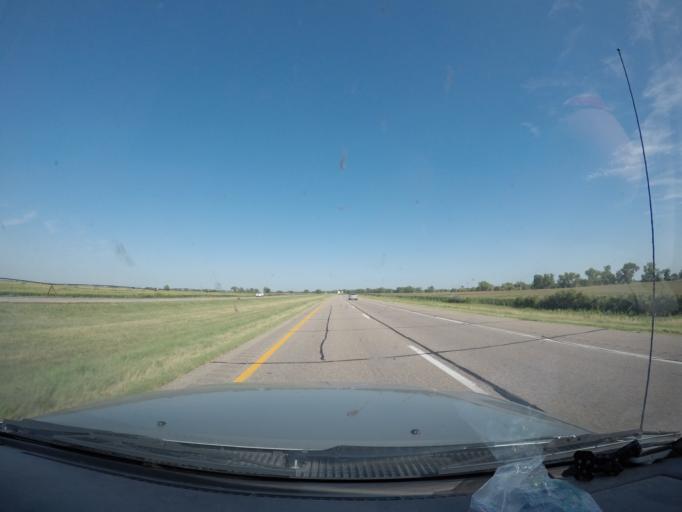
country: US
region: Nebraska
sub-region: Buffalo County
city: Kearney
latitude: 40.6884
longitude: -99.3311
